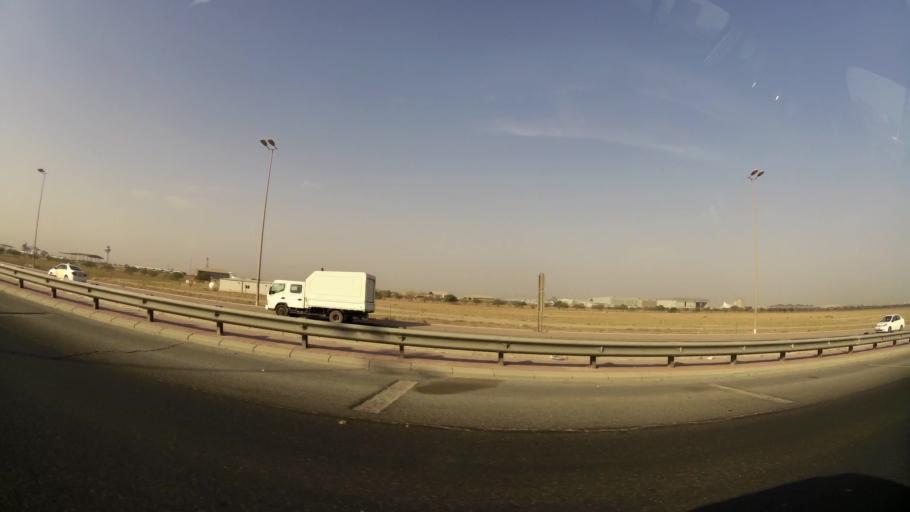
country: KW
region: Al Farwaniyah
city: Janub as Surrah
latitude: 29.2359
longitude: 47.9918
